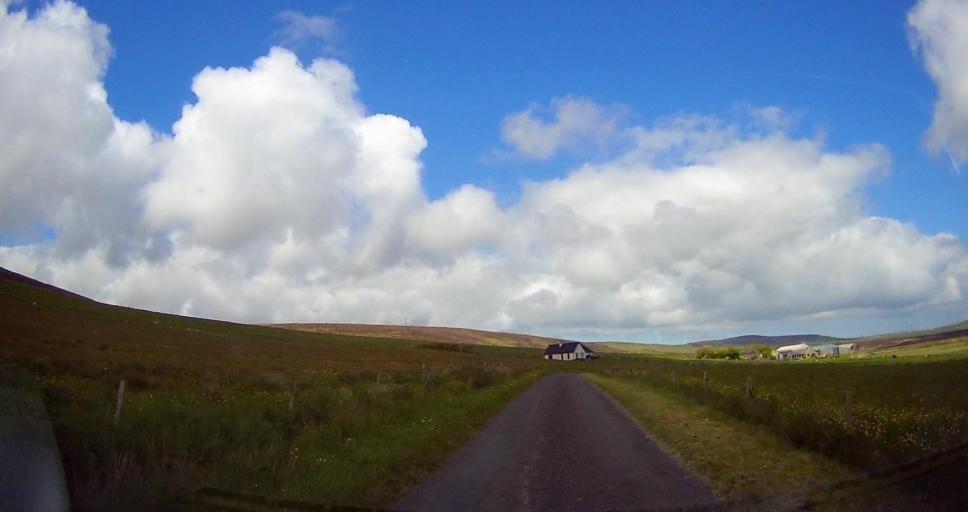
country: GB
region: Scotland
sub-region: Orkney Islands
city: Orkney
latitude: 59.0543
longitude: -3.1036
